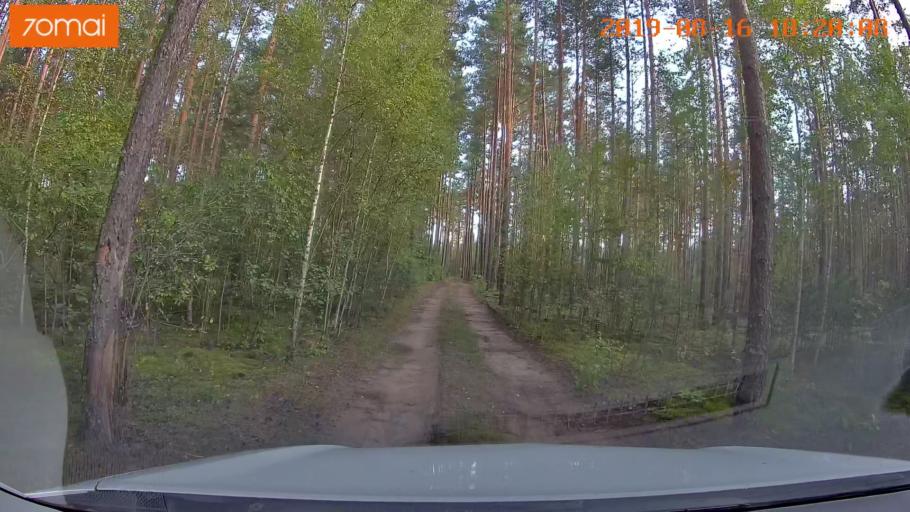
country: BY
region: Mogilev
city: Asipovichy
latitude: 53.2080
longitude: 28.6331
